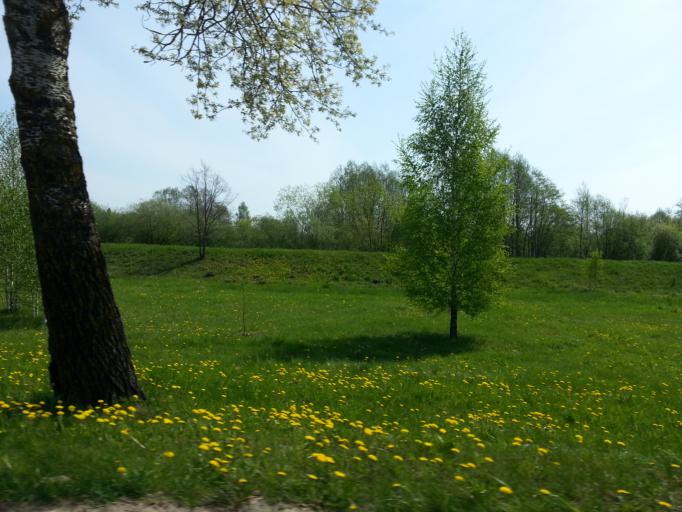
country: LT
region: Panevezys
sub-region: Panevezys City
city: Panevezys
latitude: 55.8147
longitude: 24.2707
